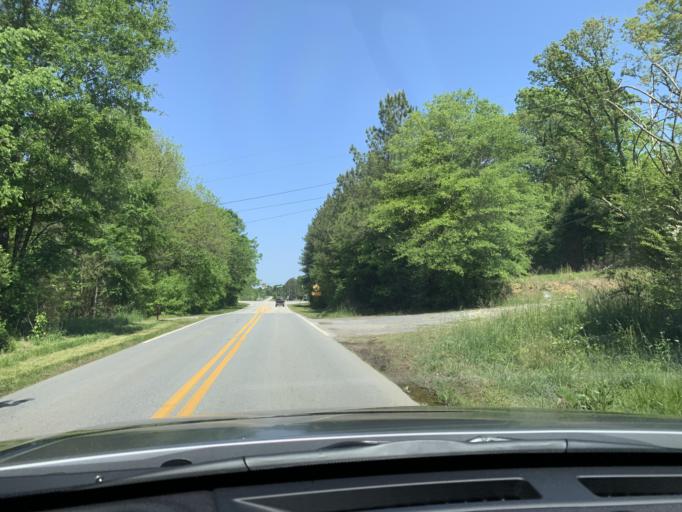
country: US
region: Georgia
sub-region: Polk County
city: Cedartown
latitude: 33.9939
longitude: -85.2313
